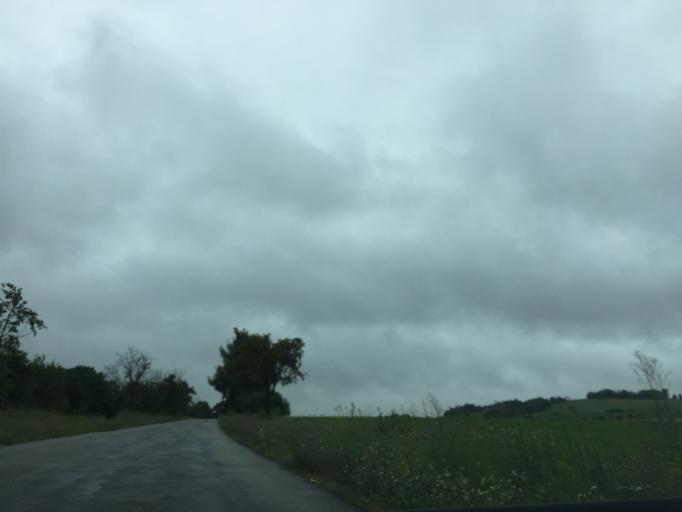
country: CZ
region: South Moravian
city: Ostrov u Macochy
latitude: 49.4001
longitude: 16.7574
